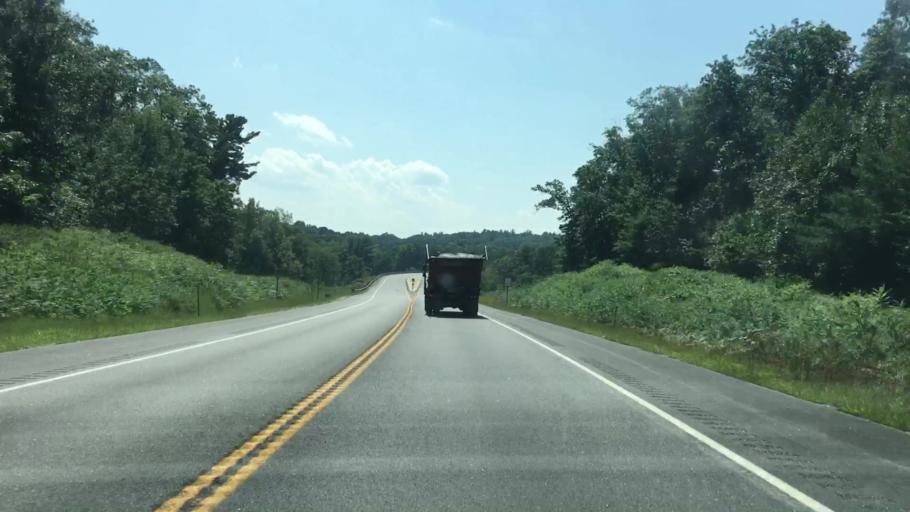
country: US
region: New Hampshire
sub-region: Rockingham County
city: Salem
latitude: 42.8180
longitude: -71.2458
